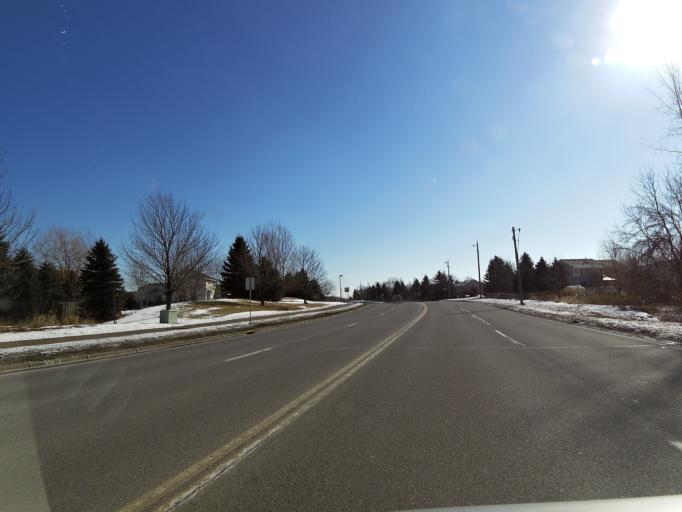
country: US
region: Minnesota
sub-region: Washington County
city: Woodbury
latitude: 44.9056
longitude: -92.9494
